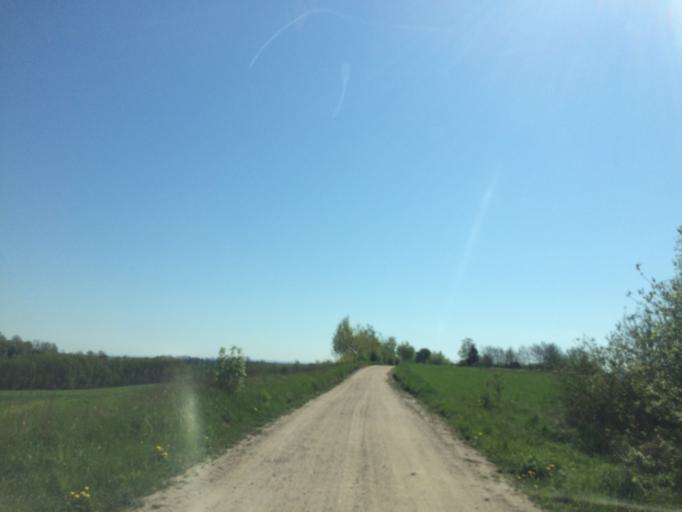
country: PL
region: Warmian-Masurian Voivodeship
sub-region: Powiat nowomiejski
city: Nowe Miasto Lubawskie
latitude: 53.4966
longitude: 19.5250
